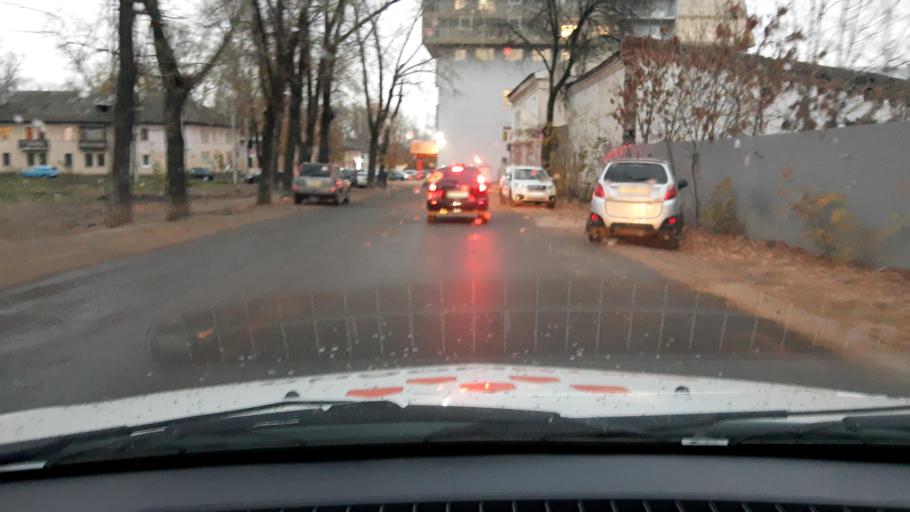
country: RU
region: Bashkortostan
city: Ufa
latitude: 54.8237
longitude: 56.0853
